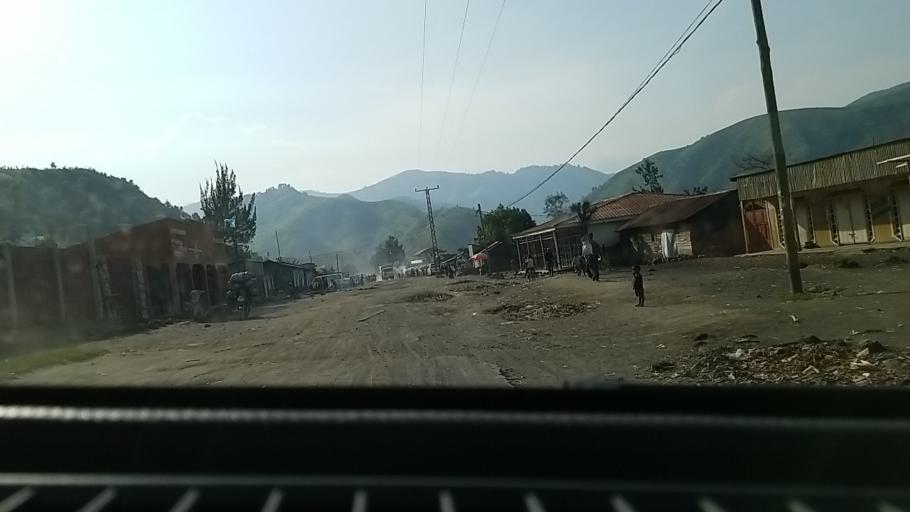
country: CD
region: Nord Kivu
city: Sake
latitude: -1.5715
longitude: 29.0545
